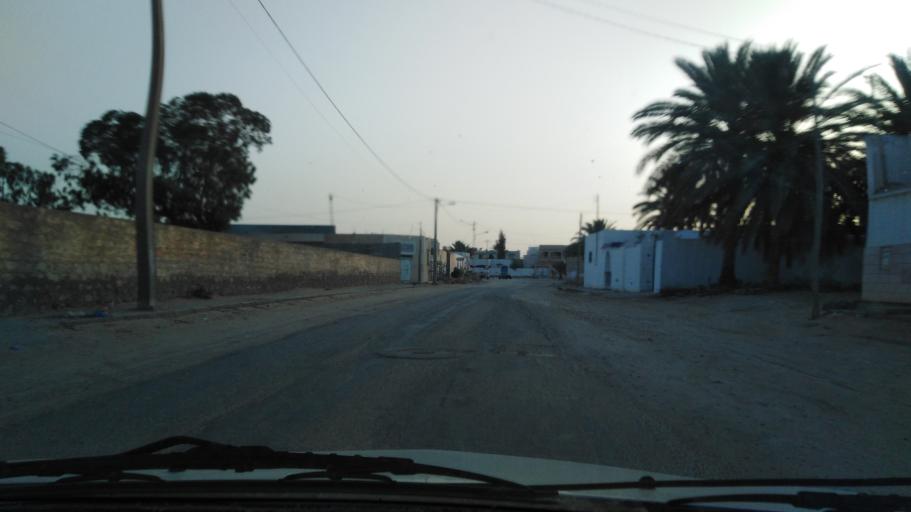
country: TN
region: Qabis
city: Gabes
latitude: 33.9571
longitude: 10.0000
